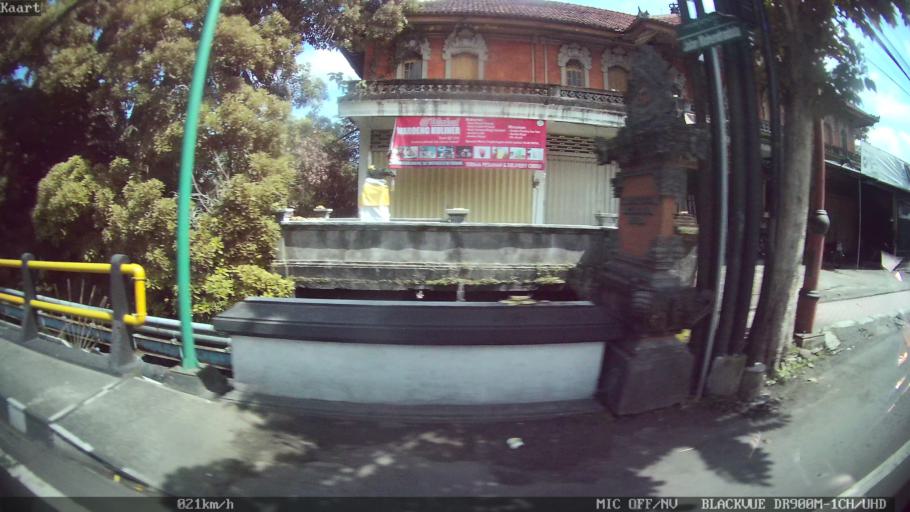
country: ID
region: Bali
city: Banjar Pesalakan
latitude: -8.5356
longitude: 115.3209
